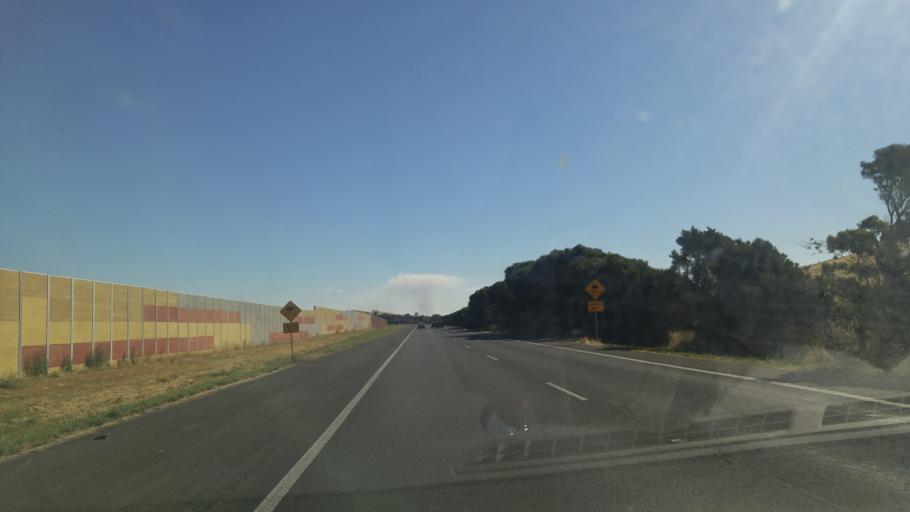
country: AU
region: Victoria
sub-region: Whittlesea
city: Whittlesea
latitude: -37.4238
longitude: 144.9895
